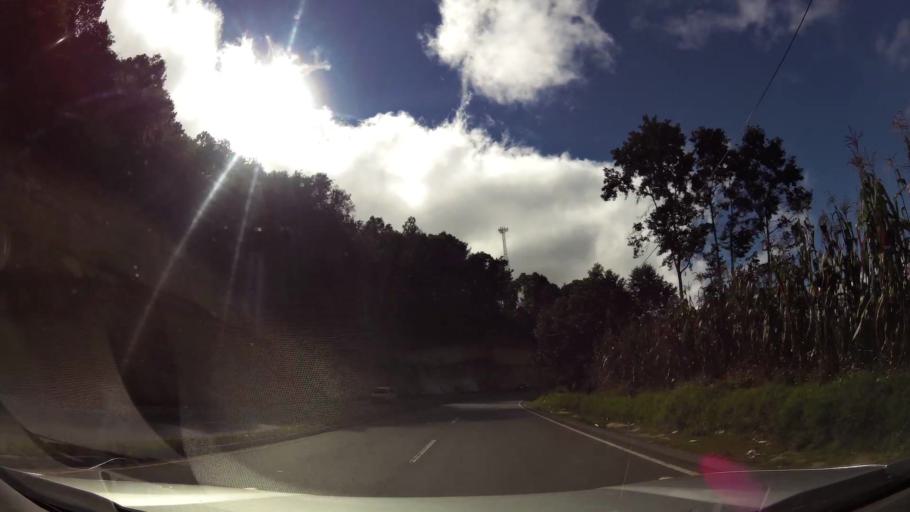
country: GT
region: Quetzaltenango
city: Salcaja
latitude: 14.8783
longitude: -91.4045
